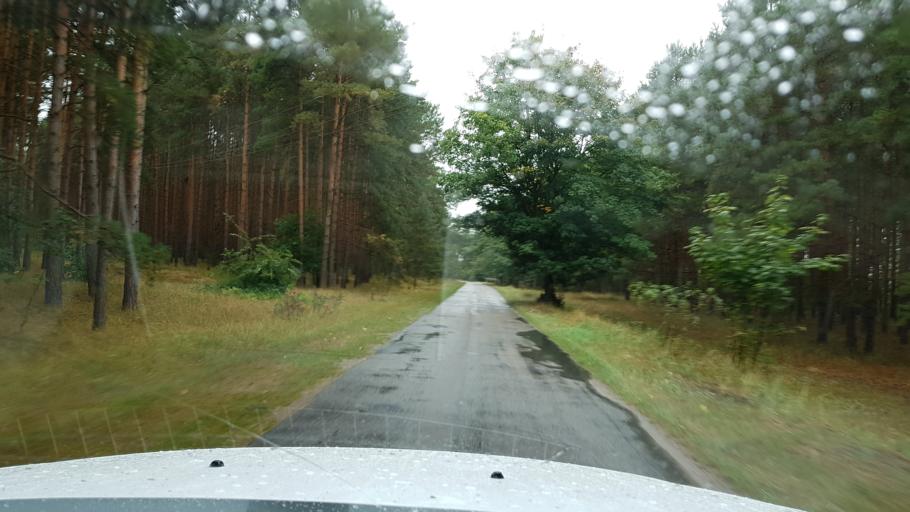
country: DE
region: Brandenburg
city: Schoneberg
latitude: 52.9473
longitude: 14.1611
